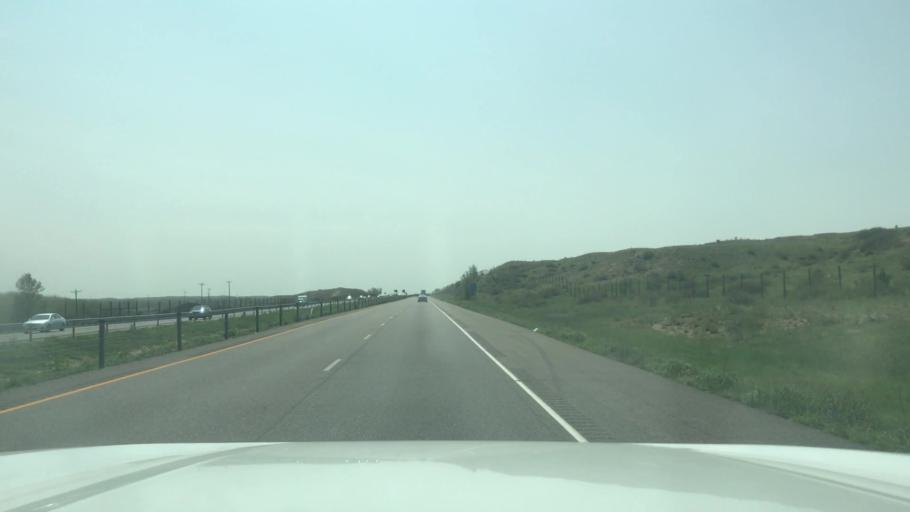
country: US
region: Colorado
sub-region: El Paso County
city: Fountain
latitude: 38.6530
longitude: -104.6977
